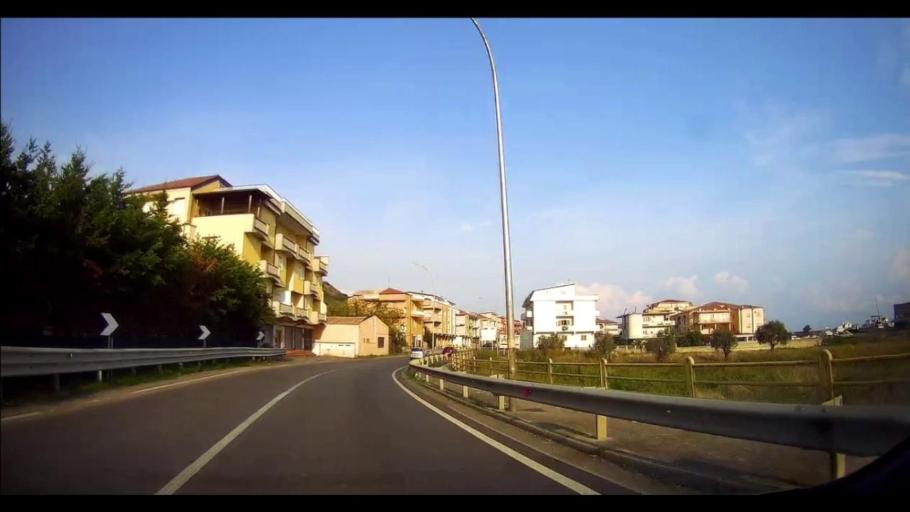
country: IT
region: Calabria
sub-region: Provincia di Cosenza
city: Cariati
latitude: 39.5046
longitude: 16.9385
